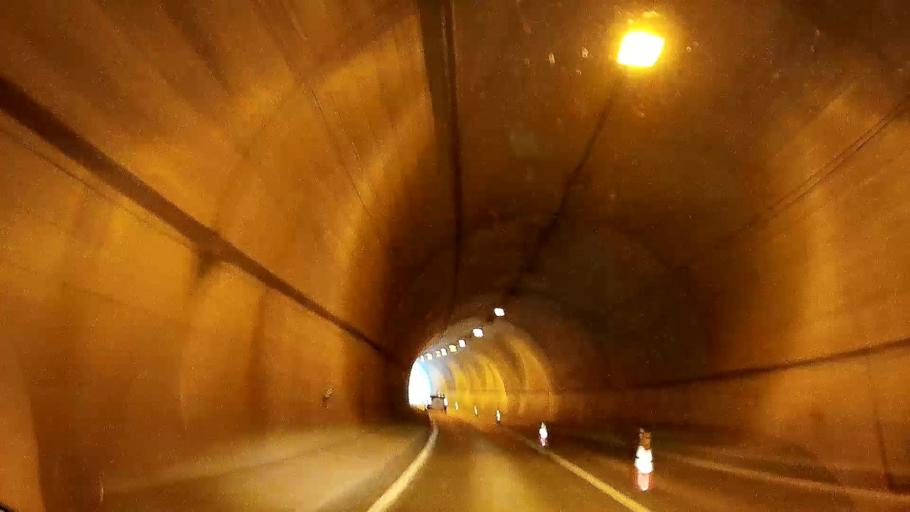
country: JP
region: Nagano
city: Toyoshina
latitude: 36.1861
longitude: 137.6265
